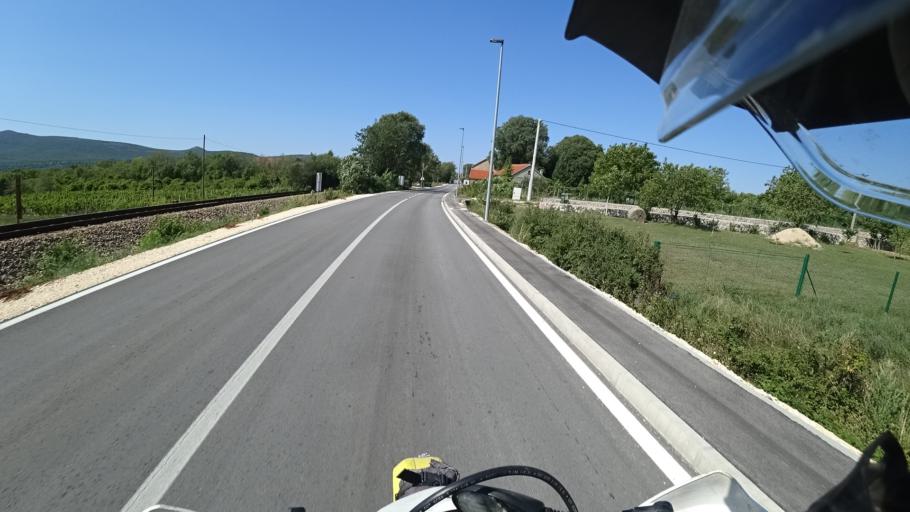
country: HR
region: Sibensko-Kniniska
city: Drnis
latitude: 43.8661
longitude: 16.1856
